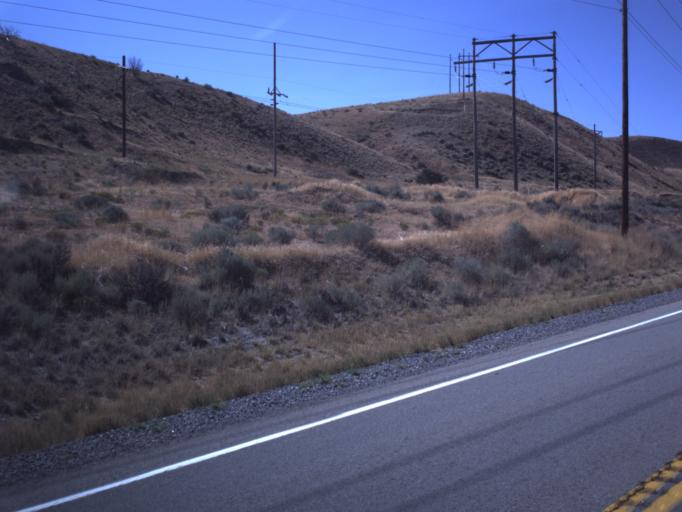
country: US
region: Utah
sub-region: Tooele County
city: Tooele
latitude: 40.4781
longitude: -112.3463
